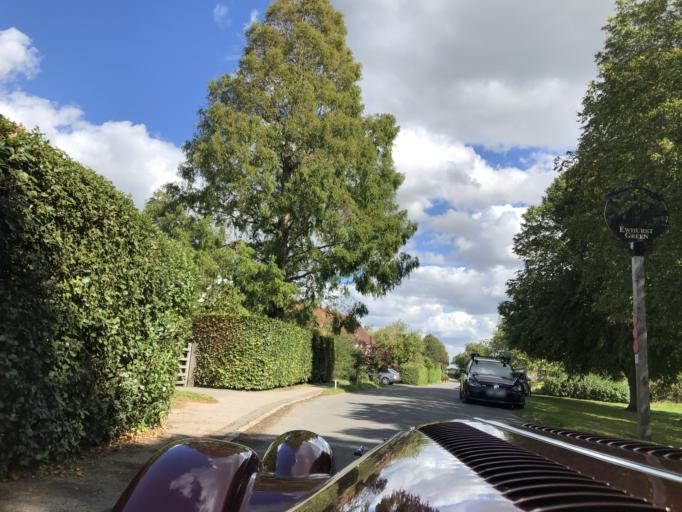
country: GB
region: England
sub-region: East Sussex
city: Northiam
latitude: 50.9925
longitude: 0.5559
